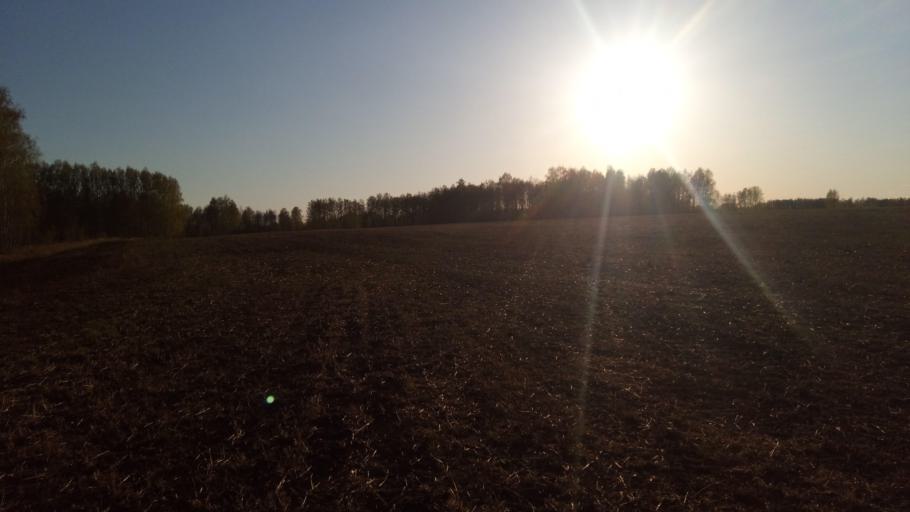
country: RU
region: Chelyabinsk
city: Timiryazevskiy
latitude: 54.9951
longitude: 60.8672
